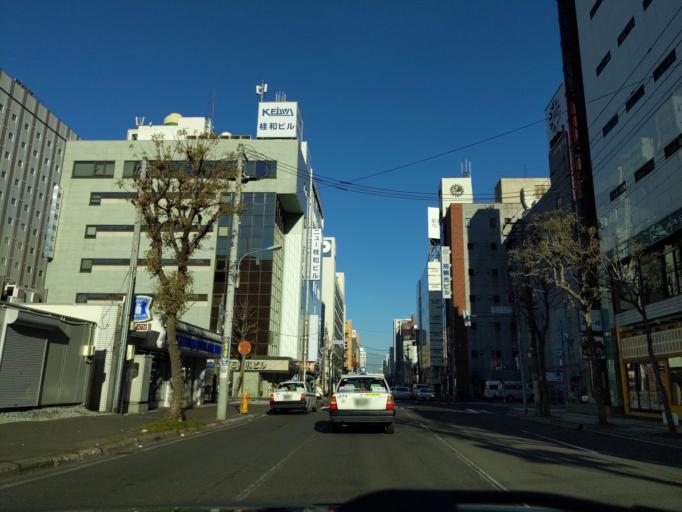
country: JP
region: Hokkaido
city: Sapporo
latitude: 43.0536
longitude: 141.3506
